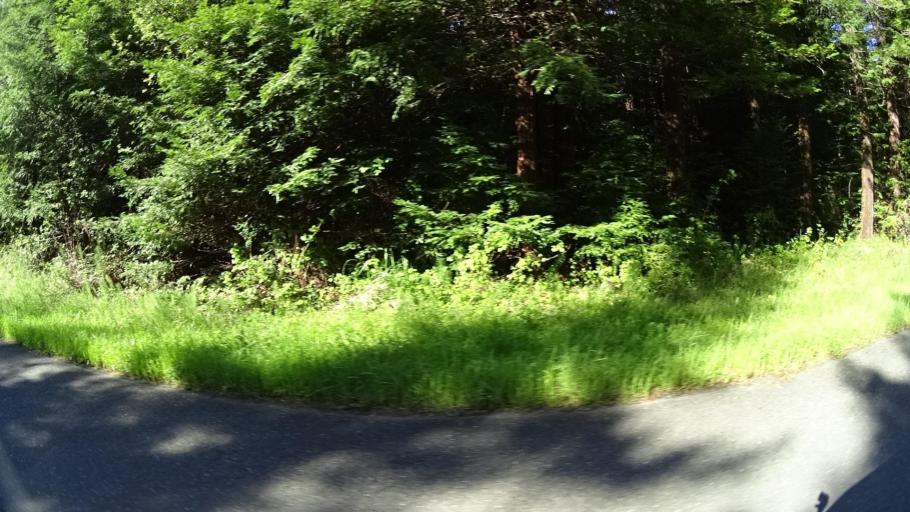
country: US
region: California
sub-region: Humboldt County
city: Rio Dell
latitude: 40.4552
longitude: -124.0315
